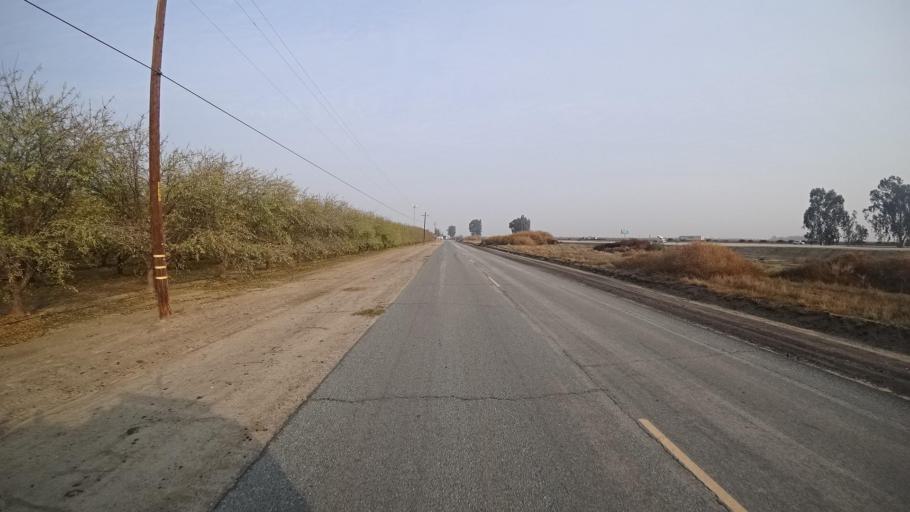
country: US
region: California
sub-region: Kern County
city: Greenfield
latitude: 35.2531
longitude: -119.0213
